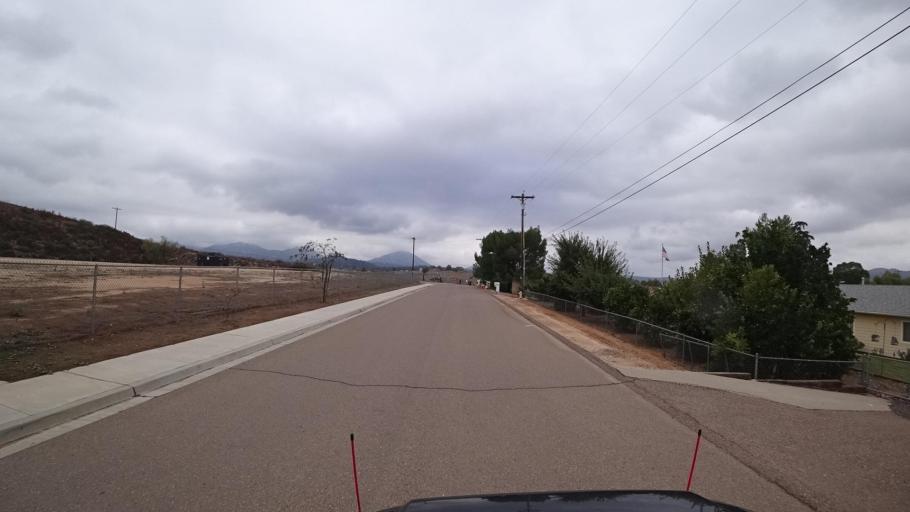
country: US
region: California
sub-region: San Diego County
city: Ramona
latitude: 33.0186
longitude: -116.8915
